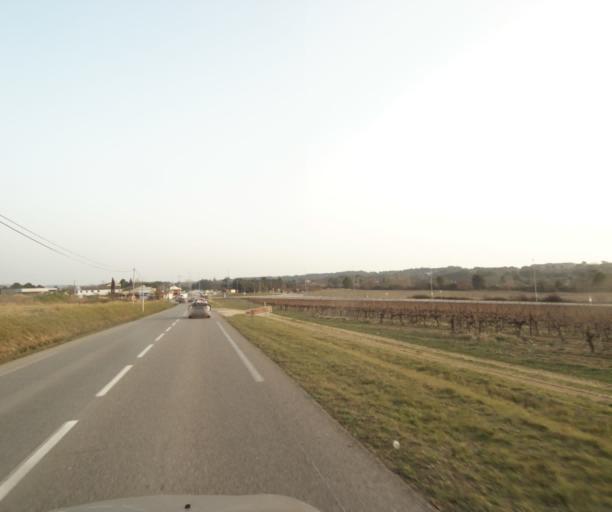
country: FR
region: Provence-Alpes-Cote d'Azur
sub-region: Departement des Bouches-du-Rhone
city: Eguilles
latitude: 43.5880
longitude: 5.3682
